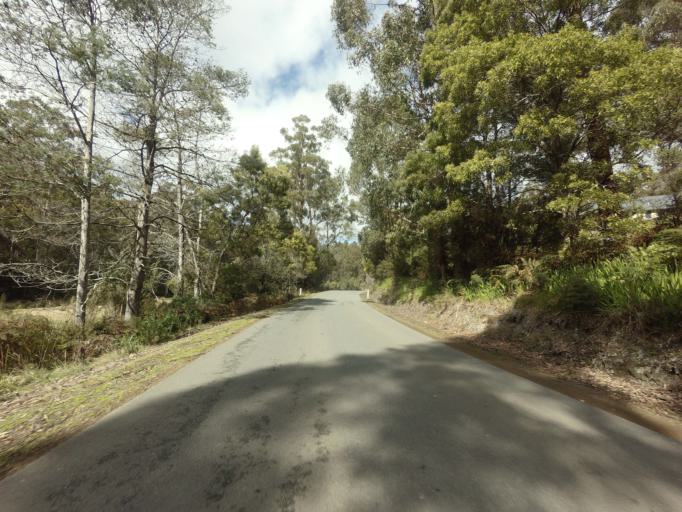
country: AU
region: Tasmania
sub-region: Huon Valley
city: Geeveston
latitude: -43.4159
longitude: 146.9643
